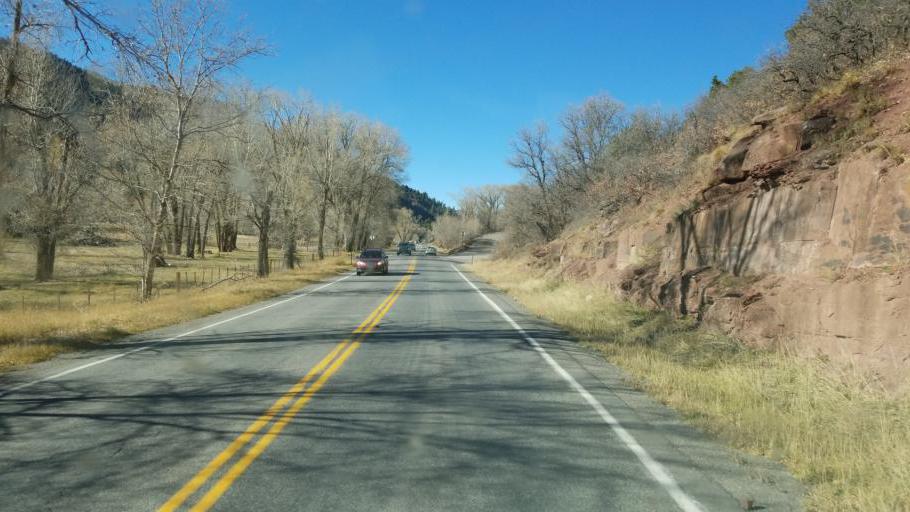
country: US
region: Colorado
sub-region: Ouray County
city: Ouray
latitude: 38.0495
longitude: -107.6833
